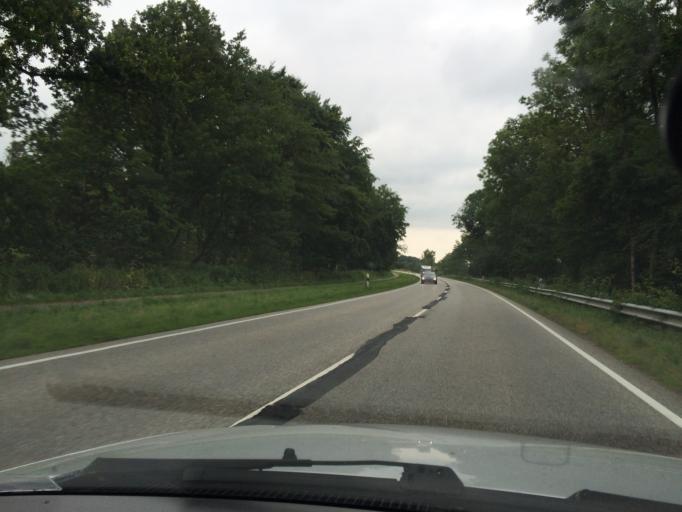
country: DE
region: Schleswig-Holstein
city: Oeversee
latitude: 54.6676
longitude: 9.4435
